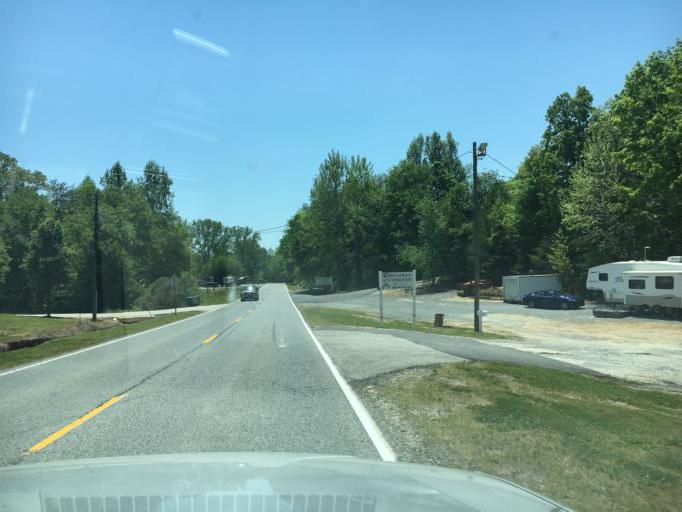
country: US
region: South Carolina
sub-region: Cherokee County
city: Blacksburg
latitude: 35.1377
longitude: -81.5805
